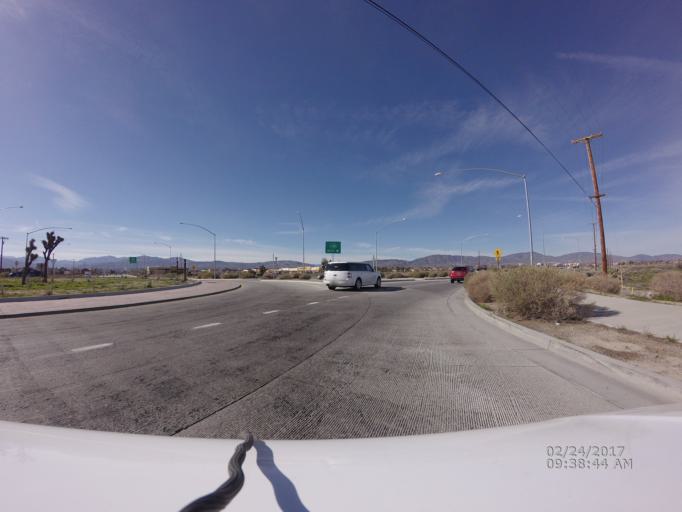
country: US
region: California
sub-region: Los Angeles County
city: Palmdale
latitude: 34.5803
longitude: -118.0452
